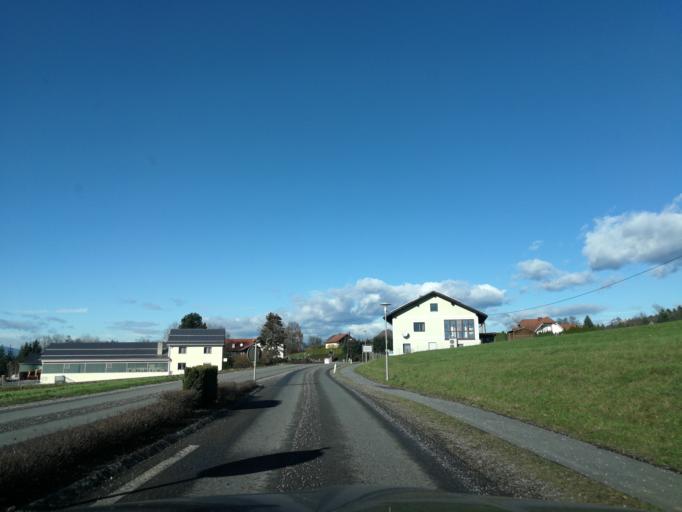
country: AT
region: Styria
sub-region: Politischer Bezirk Weiz
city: Hofstatten an der Raab
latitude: 47.0805
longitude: 15.7429
